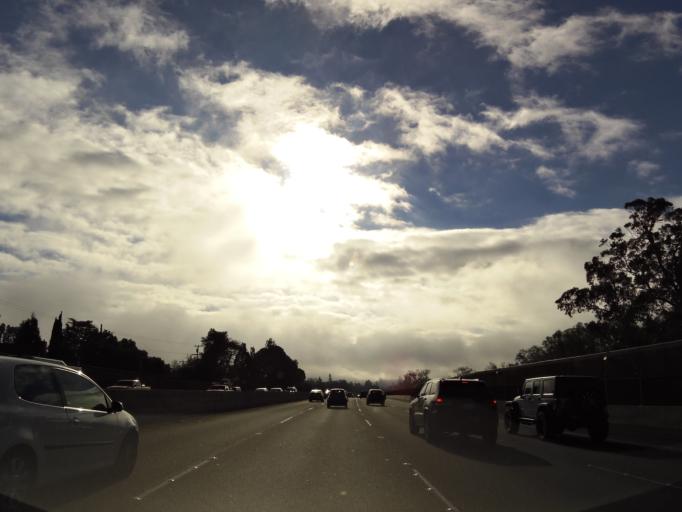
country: US
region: California
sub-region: Marin County
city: San Rafael
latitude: 37.9842
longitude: -122.5234
